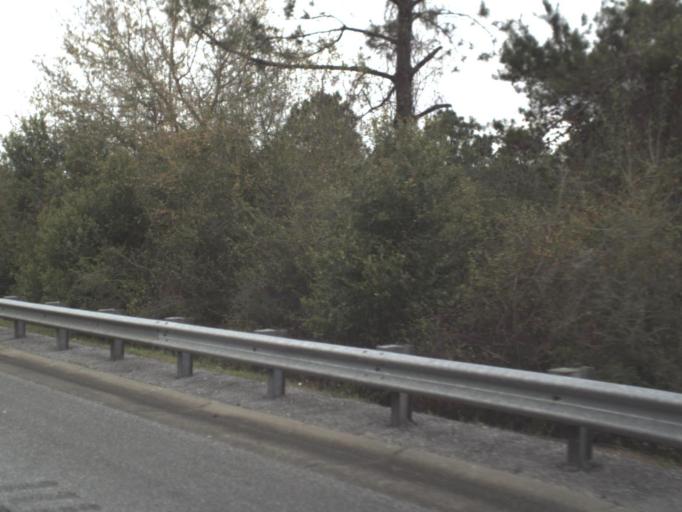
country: US
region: Florida
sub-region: Okaloosa County
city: Crestview
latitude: 30.7194
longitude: -86.6016
